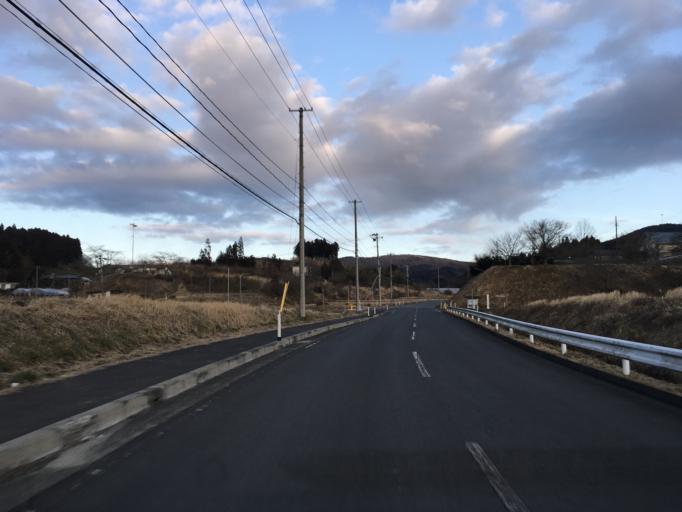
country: JP
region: Iwate
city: Ichinoseki
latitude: 38.8668
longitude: 141.3559
